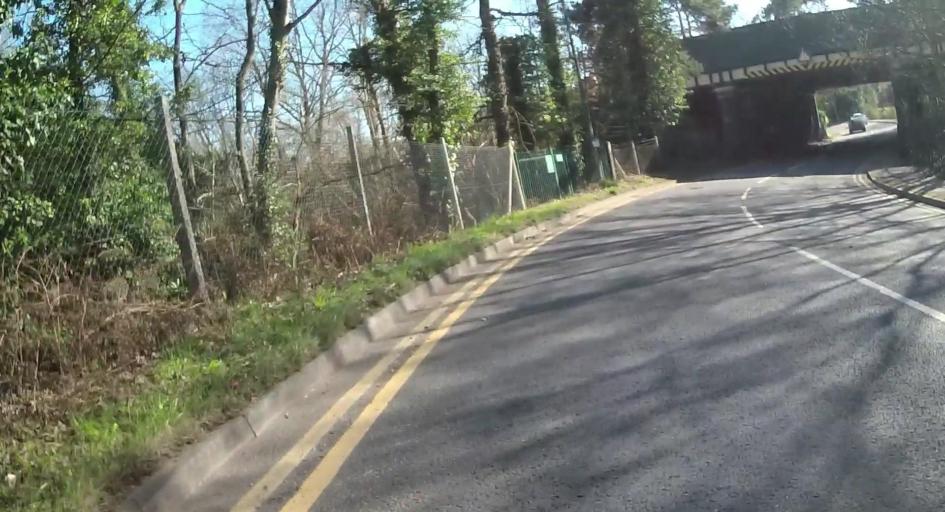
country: GB
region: England
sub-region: Royal Borough of Windsor and Maidenhead
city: Ascot
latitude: 51.4057
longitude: -0.6719
